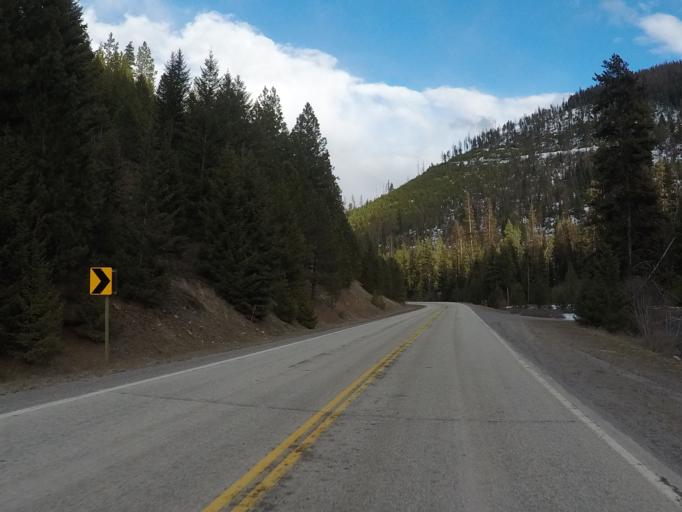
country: US
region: Montana
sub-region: Missoula County
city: Frenchtown
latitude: 46.7658
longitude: -114.4801
